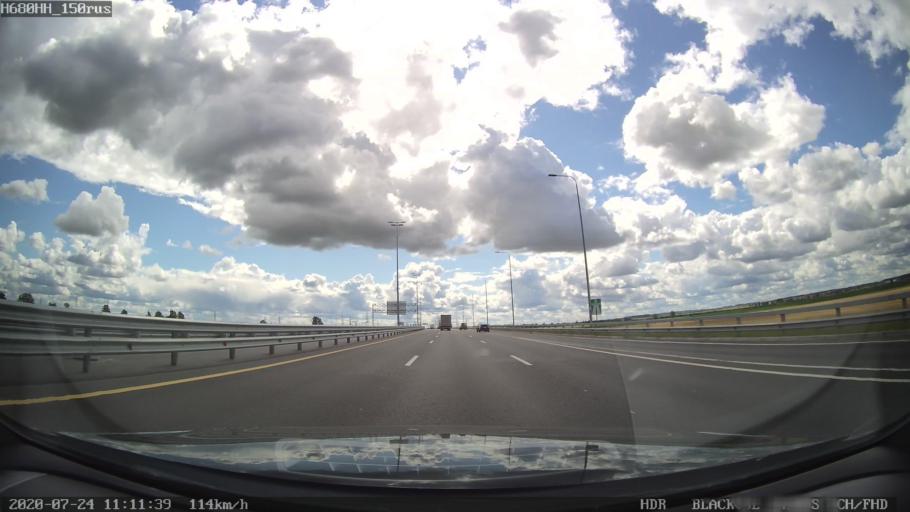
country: RU
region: Leningrad
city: Fedorovskoye
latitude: 59.7198
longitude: 30.5192
